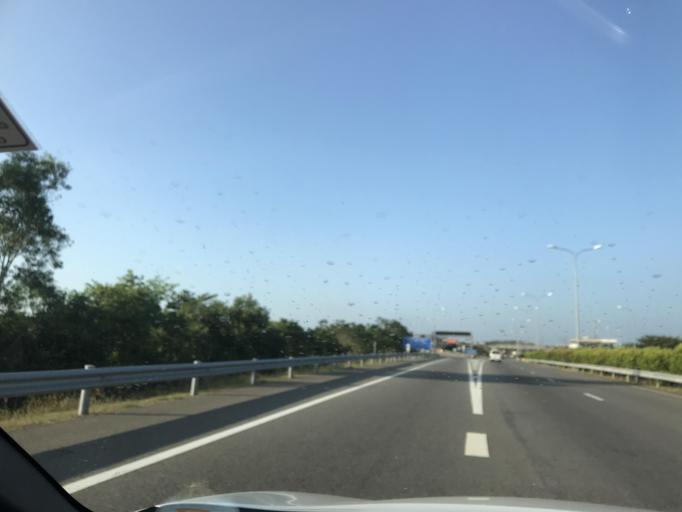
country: LK
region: Western
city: Ja Ela
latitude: 7.0779
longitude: 79.8774
